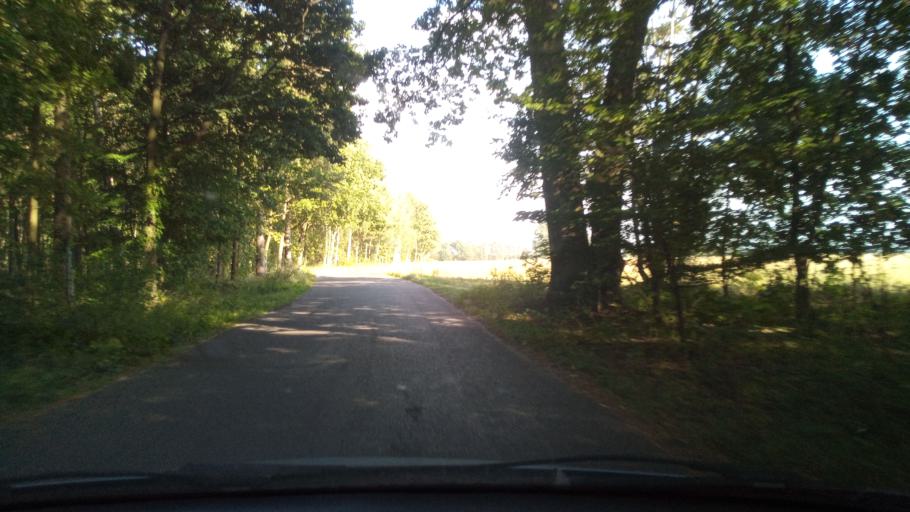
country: PL
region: Lodz Voivodeship
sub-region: Powiat piotrkowski
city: Sulejow
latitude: 51.4102
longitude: 19.8352
